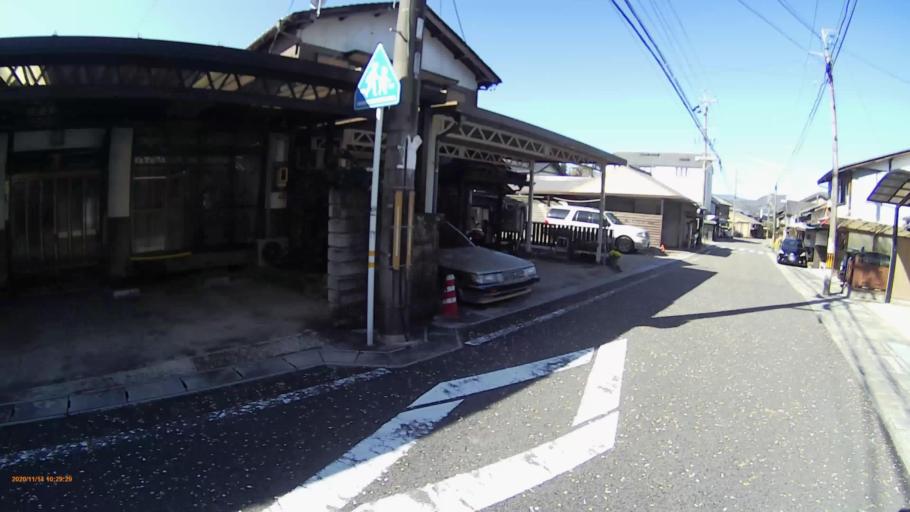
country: JP
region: Gifu
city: Nakatsugawa
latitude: 35.5105
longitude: 137.5323
